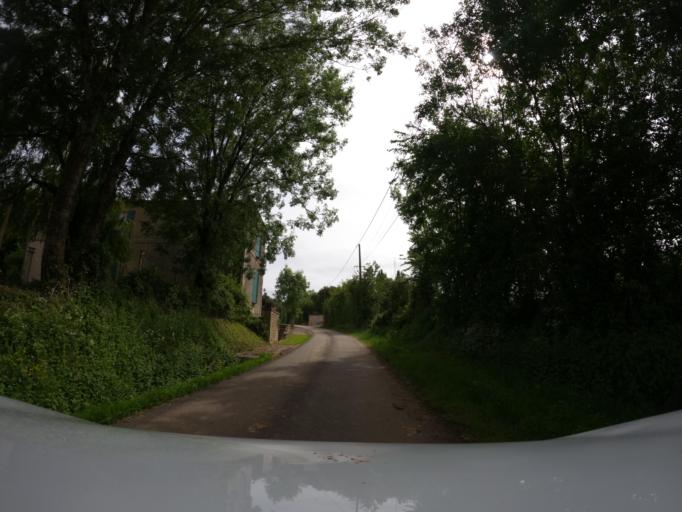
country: FR
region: Pays de la Loire
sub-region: Departement de la Vendee
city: Saint-Hilaire-des-Loges
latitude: 46.4975
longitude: -0.6510
